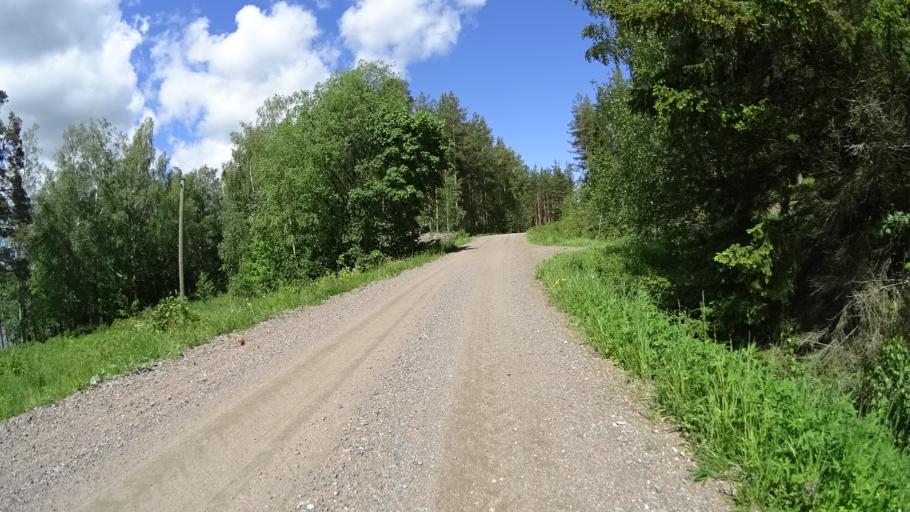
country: FI
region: Uusimaa
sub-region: Raaseporin
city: Karis
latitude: 60.1308
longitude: 23.6175
